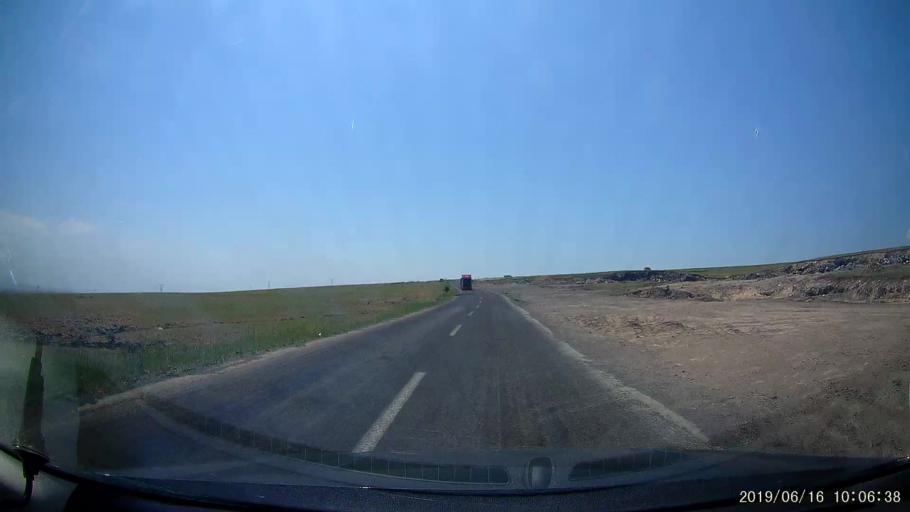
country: TR
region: Kars
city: Digor
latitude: 40.2527
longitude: 43.5446
